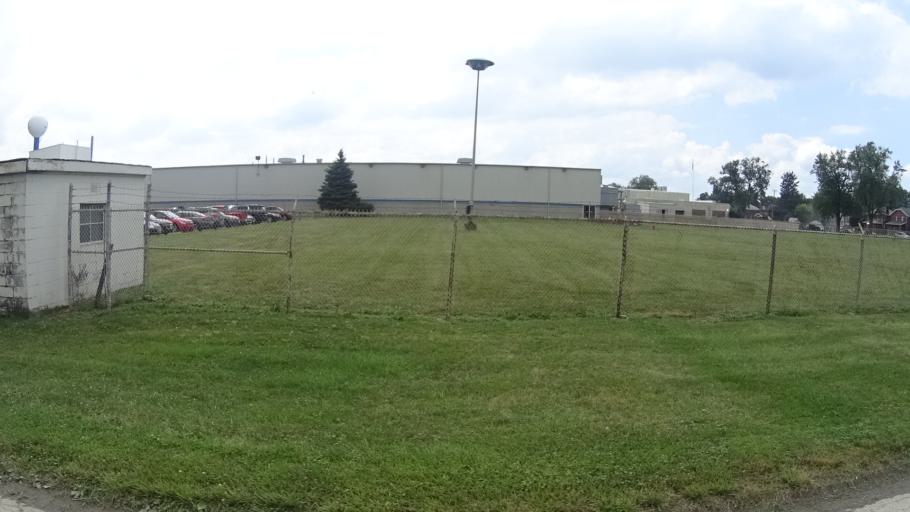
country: US
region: Ohio
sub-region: Erie County
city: Sandusky
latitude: 41.4451
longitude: -82.7408
